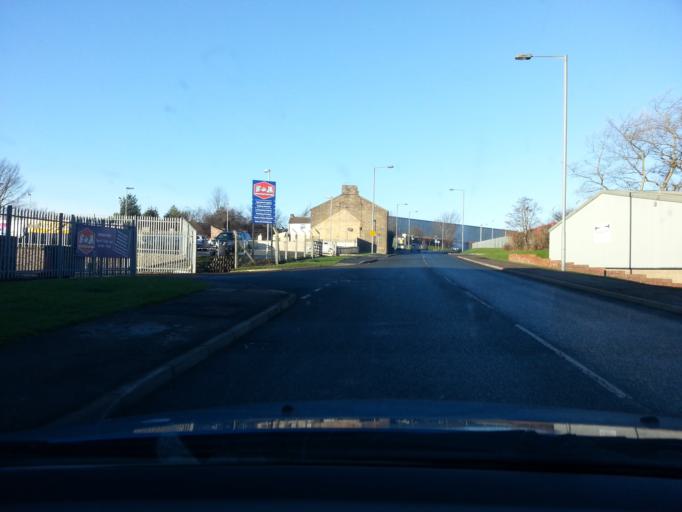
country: GB
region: England
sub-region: County Durham
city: Crook
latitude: 54.7060
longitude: -1.7501
